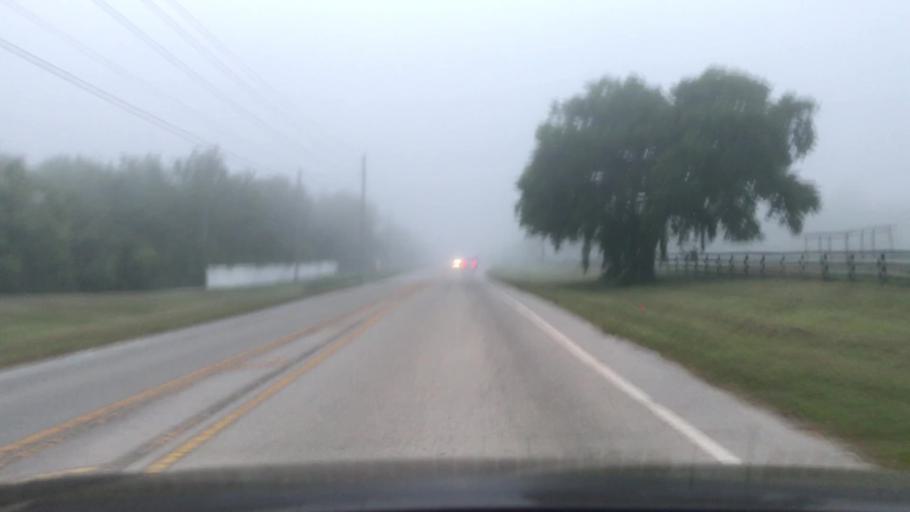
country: US
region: Florida
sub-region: Sarasota County
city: Lake Sarasota
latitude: 27.3243
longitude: -82.4224
